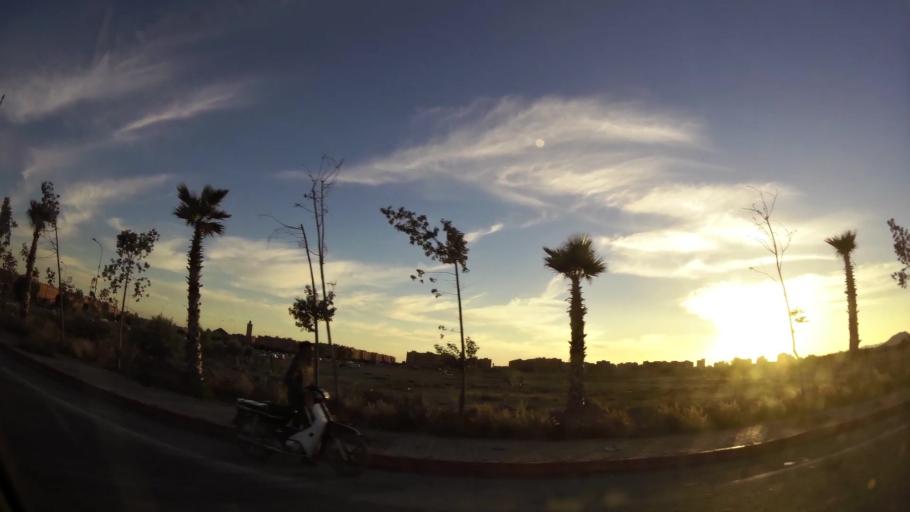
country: MA
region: Marrakech-Tensift-Al Haouz
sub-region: Marrakech
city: Marrakesh
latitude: 31.7548
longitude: -8.1114
